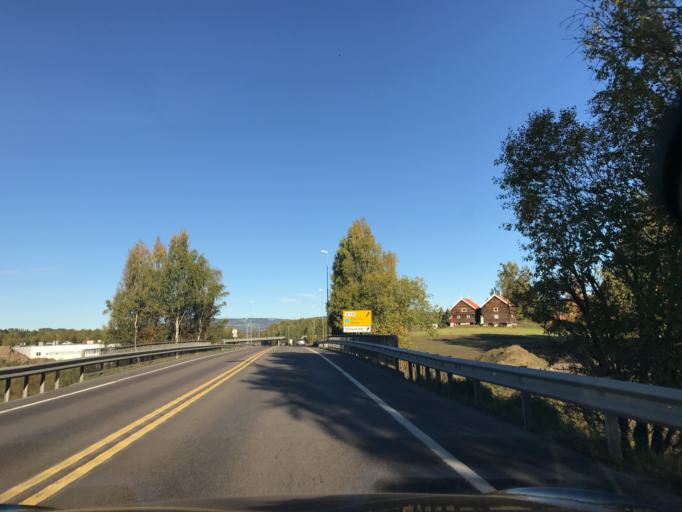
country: NO
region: Hedmark
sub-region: Hamar
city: Hamar
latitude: 60.7969
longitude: 11.1206
